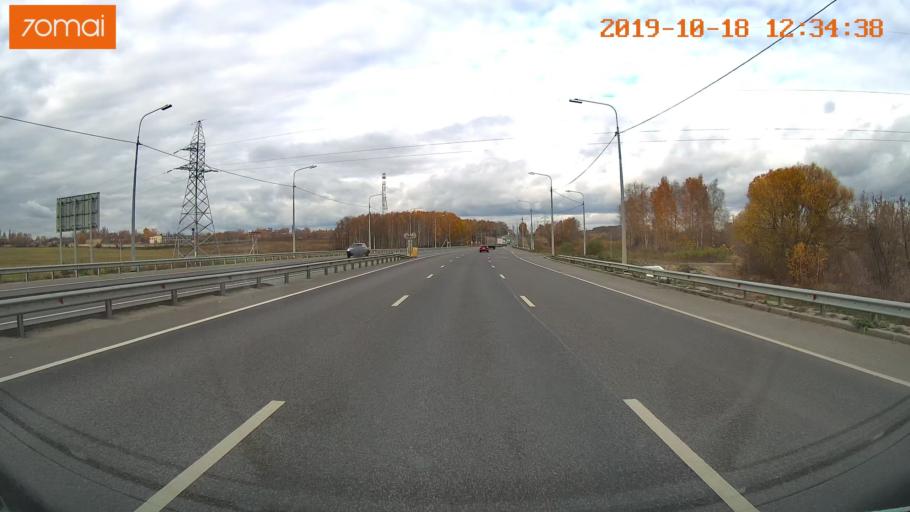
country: RU
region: Rjazan
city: Ryazan'
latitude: 54.6162
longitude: 39.6373
